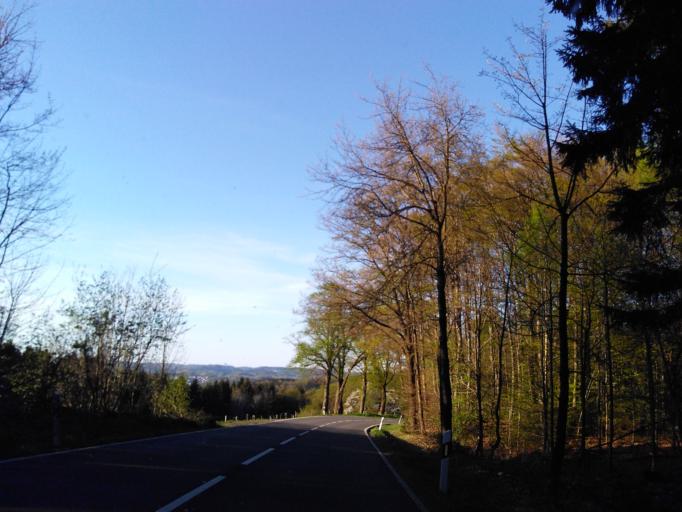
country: DE
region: North Rhine-Westphalia
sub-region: Regierungsbezirk Koln
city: Engelskirchen
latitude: 50.9667
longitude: 7.4535
